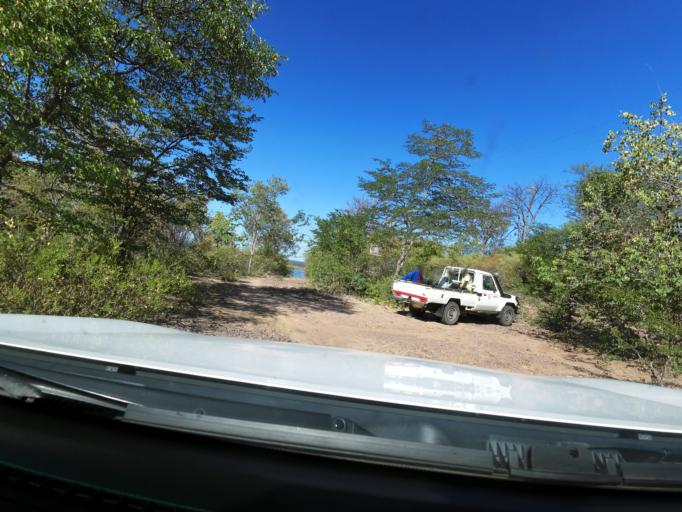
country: ZW
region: Matabeleland North
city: Kamativi Mine
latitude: -17.9433
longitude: 27.0767
